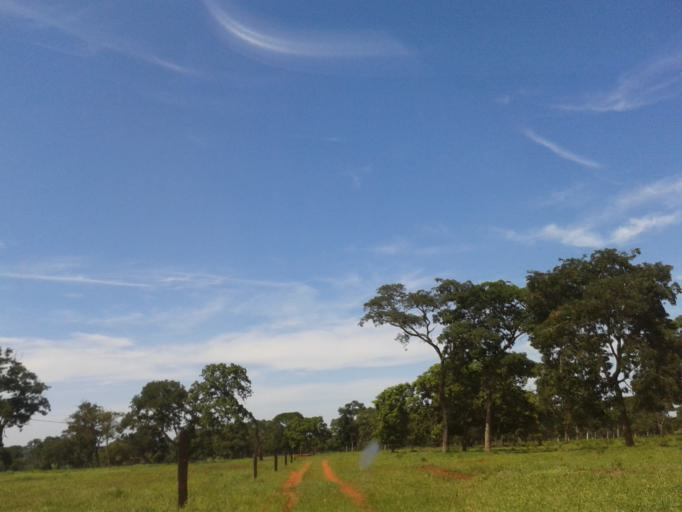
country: BR
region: Minas Gerais
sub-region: Santa Vitoria
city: Santa Vitoria
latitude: -19.1610
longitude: -50.5064
